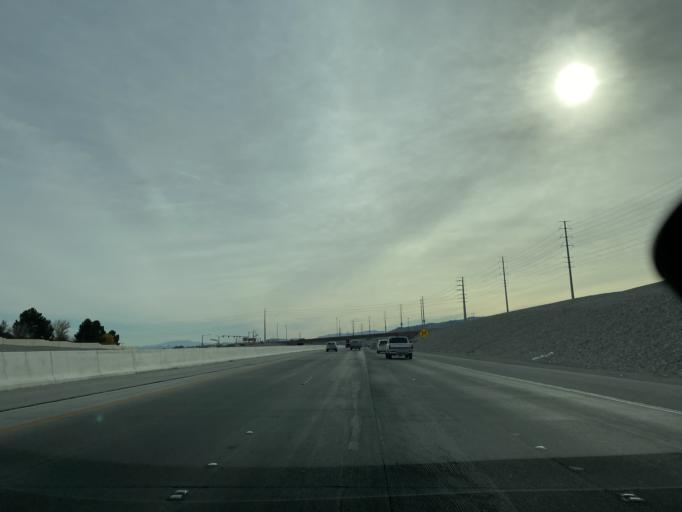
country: US
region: Nevada
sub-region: Clark County
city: Summerlin South
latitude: 36.1952
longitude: -115.3425
